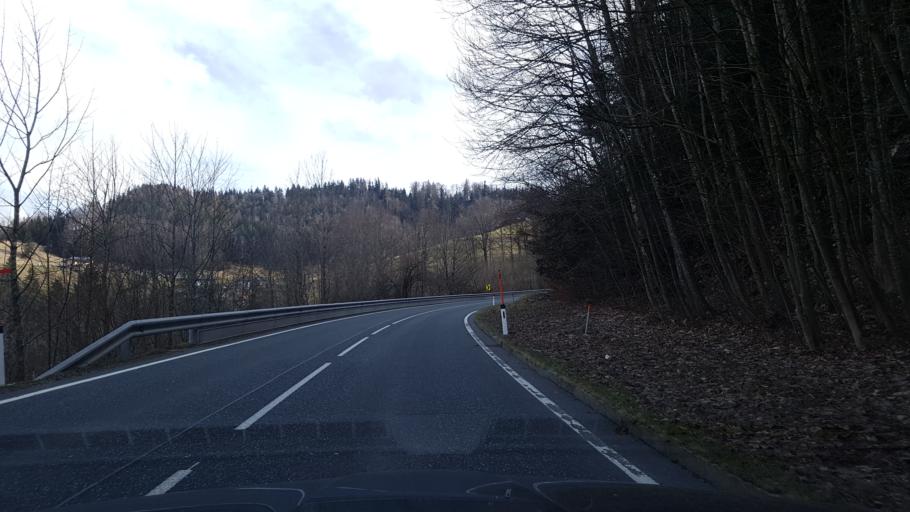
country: AT
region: Salzburg
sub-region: Politischer Bezirk Hallein
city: Hallein
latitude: 47.6610
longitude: 13.0964
